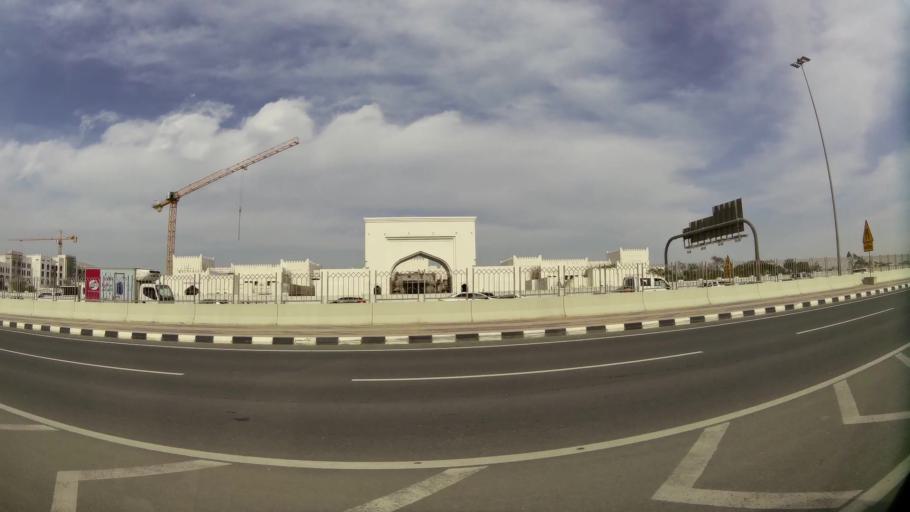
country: QA
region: Baladiyat ar Rayyan
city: Ar Rayyan
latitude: 25.3006
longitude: 51.4737
